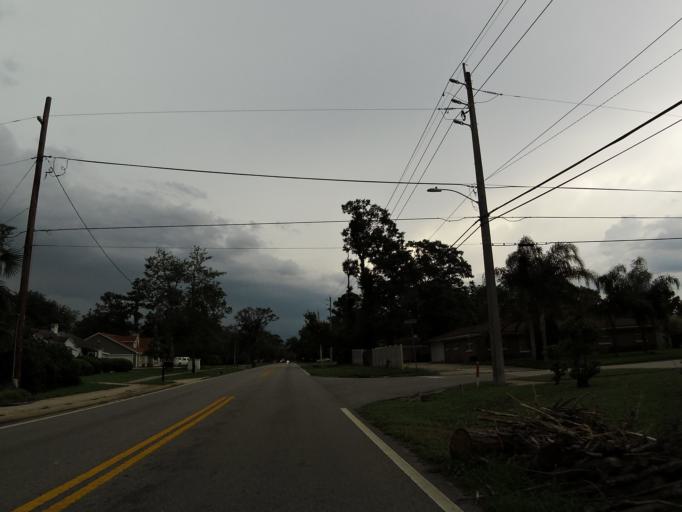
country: US
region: Florida
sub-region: Duval County
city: Jacksonville
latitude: 30.2760
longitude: -81.5891
